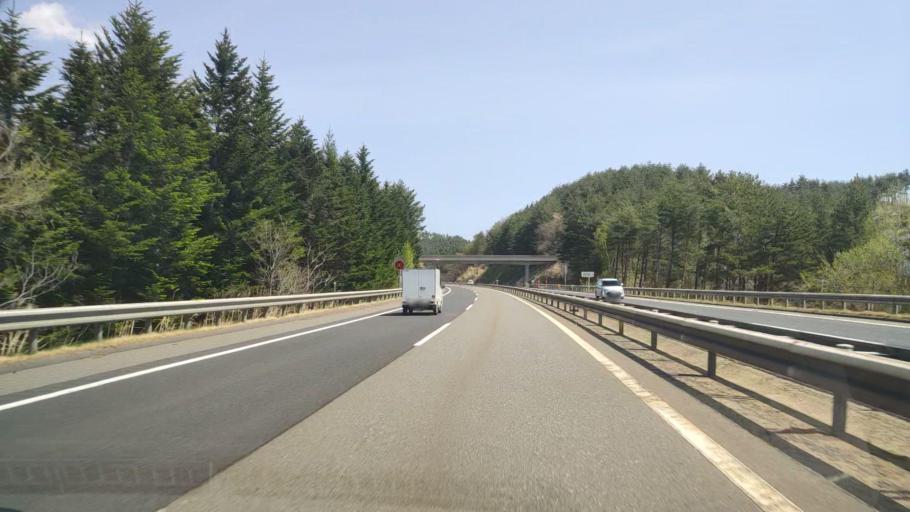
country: JP
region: Iwate
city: Ichinohe
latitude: 40.2903
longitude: 141.4180
